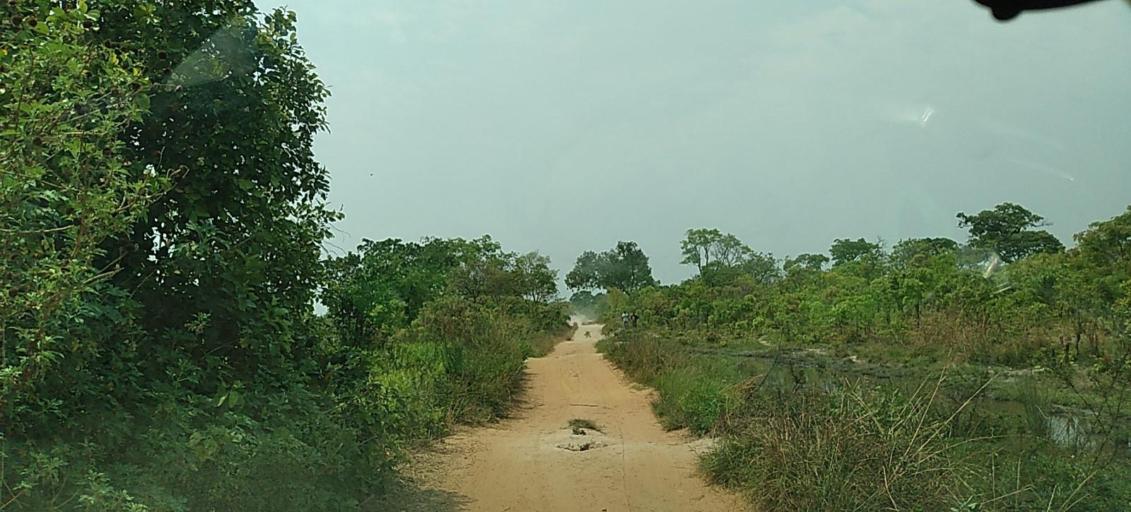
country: ZM
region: North-Western
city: Kabompo
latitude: -13.4752
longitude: 24.4537
